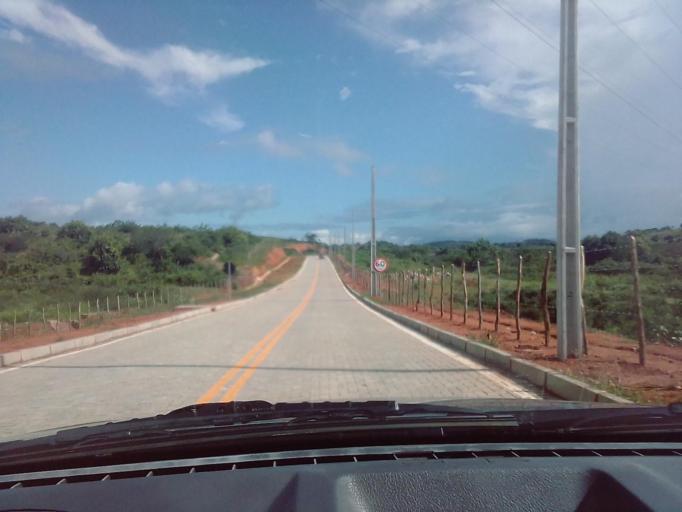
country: BR
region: Pernambuco
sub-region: Jaboatao Dos Guararapes
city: Jaboatao dos Guararapes
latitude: -8.1024
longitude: -35.0338
